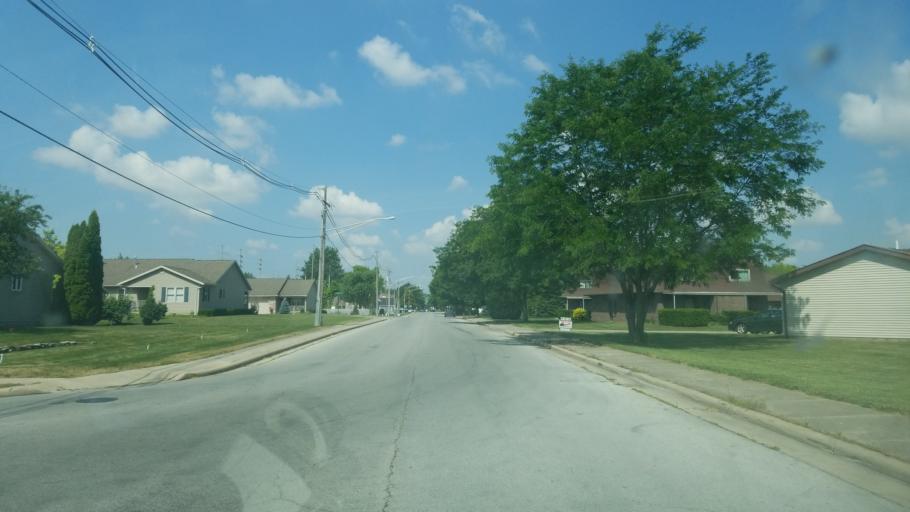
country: US
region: Ohio
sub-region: Auglaize County
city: Wapakoneta
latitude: 40.5700
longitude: -84.1765
